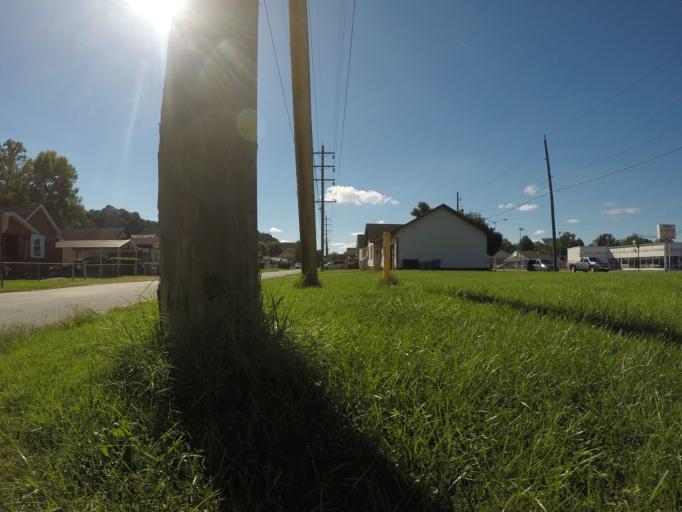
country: US
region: Ohio
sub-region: Lawrence County
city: Burlington
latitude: 38.3984
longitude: -82.5196
